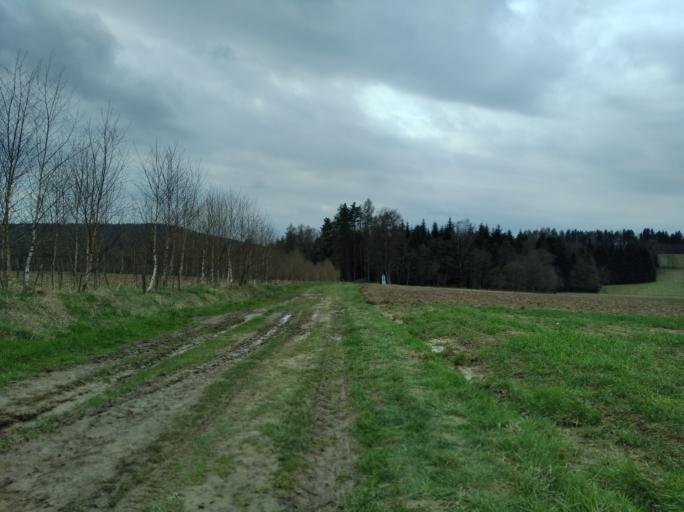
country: PL
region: Subcarpathian Voivodeship
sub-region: Powiat strzyzowski
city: Wysoka Strzyzowska
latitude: 49.8066
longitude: 21.7737
